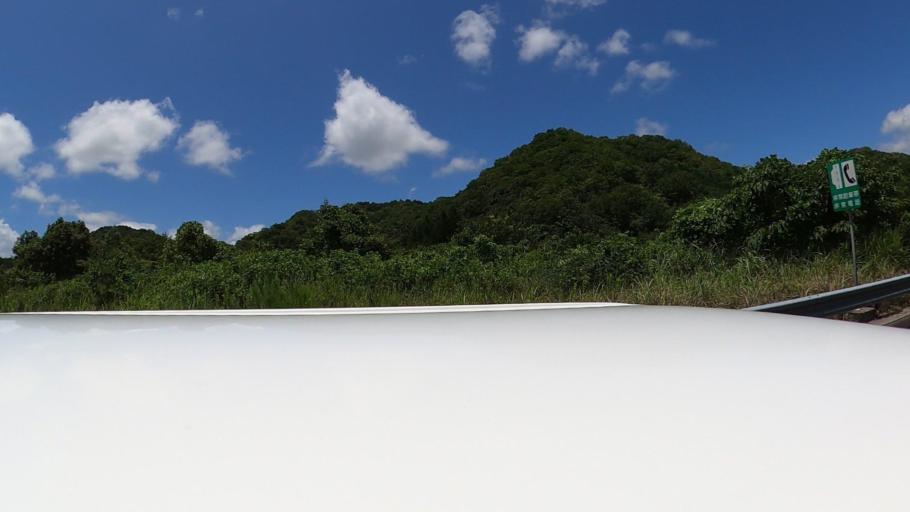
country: JP
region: Miyazaki
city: Nobeoka
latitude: 32.4590
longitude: 131.6152
